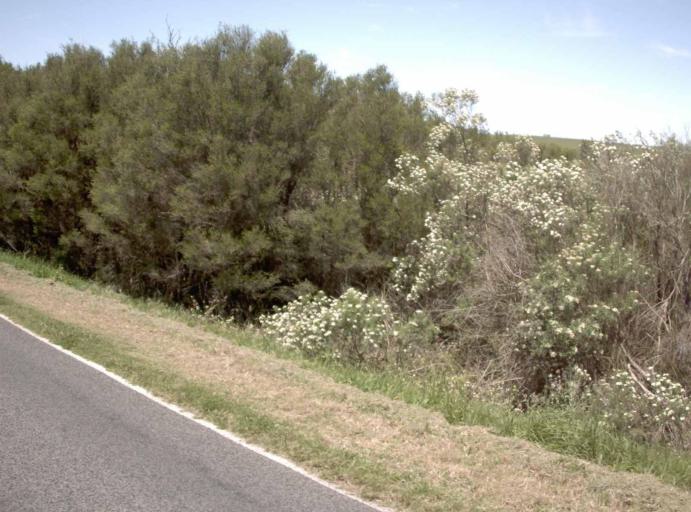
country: AU
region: Victoria
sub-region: Bass Coast
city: North Wonthaggi
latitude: -38.7673
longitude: 146.1559
